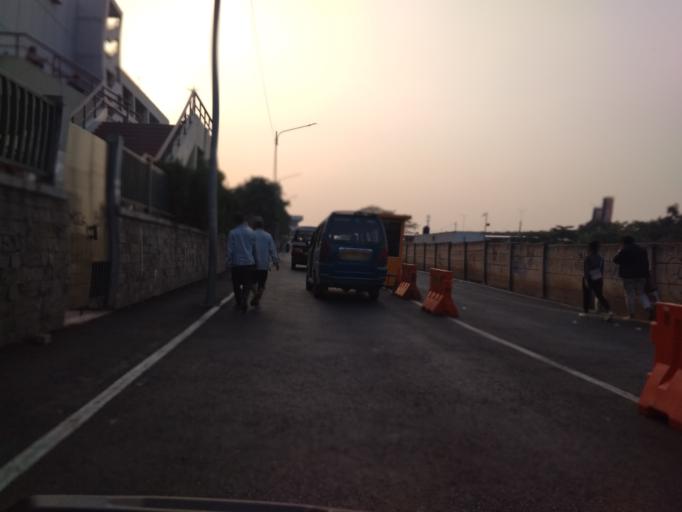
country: ID
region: West Java
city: Depok
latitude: -6.3920
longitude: 106.8238
